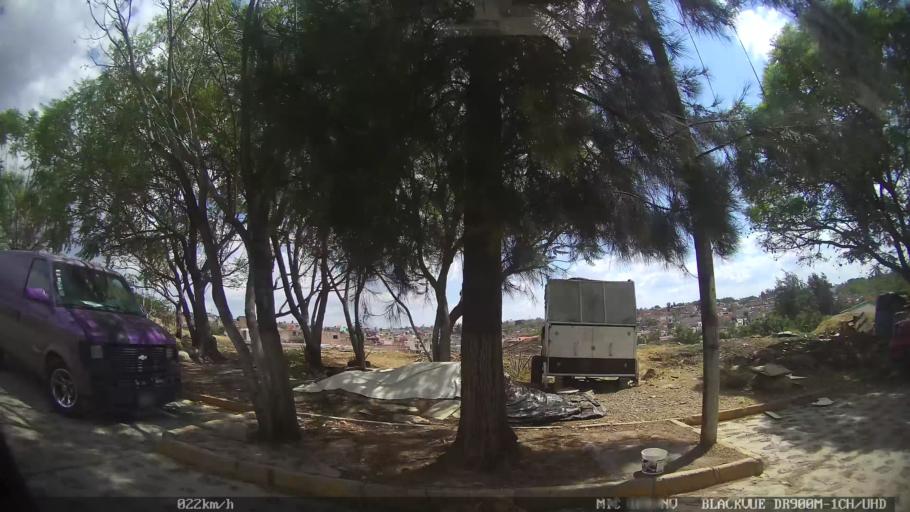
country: MX
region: Jalisco
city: Tlaquepaque
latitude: 20.6826
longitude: -103.2657
